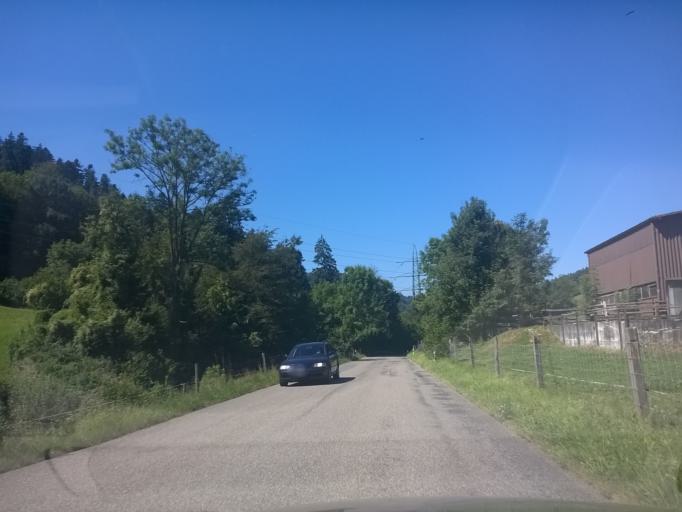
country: CH
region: Zurich
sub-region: Bezirk Winterthur
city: Pfungen
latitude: 47.5072
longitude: 8.6554
